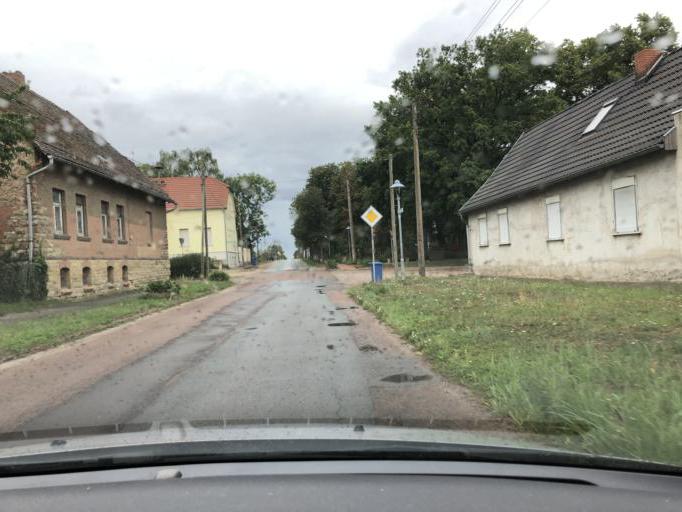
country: DE
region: Saxony-Anhalt
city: Wulfen
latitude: 51.8413
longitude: 11.8799
